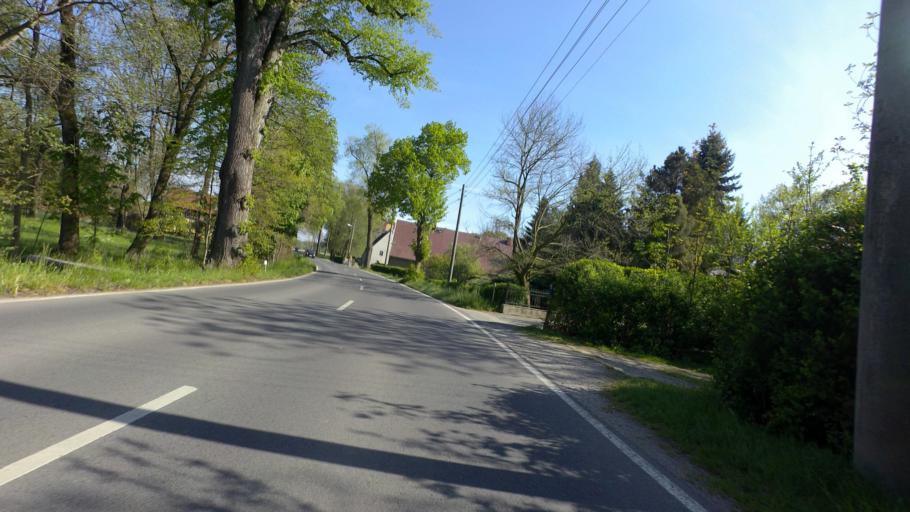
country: DE
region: Saxony
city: Kamenz
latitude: 51.2518
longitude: 14.1198
